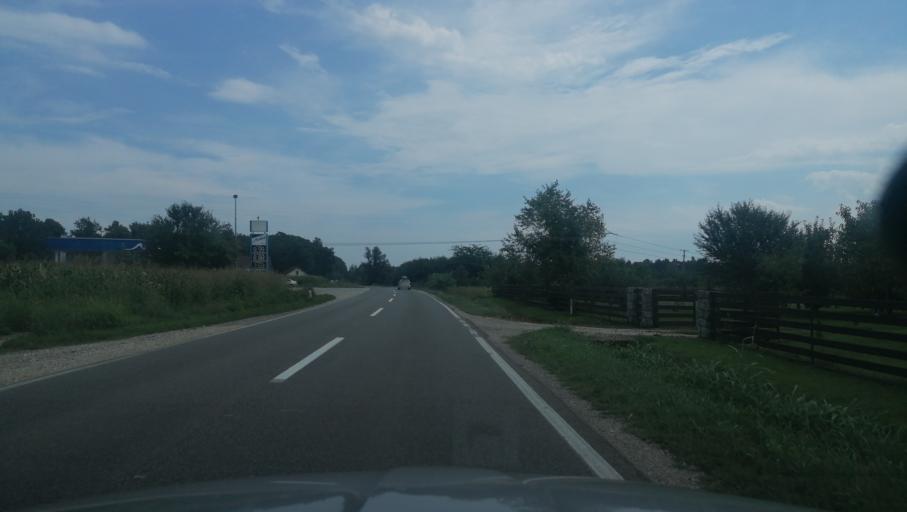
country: BA
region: Federation of Bosnia and Herzegovina
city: Orasje
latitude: 44.9320
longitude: 18.7006
